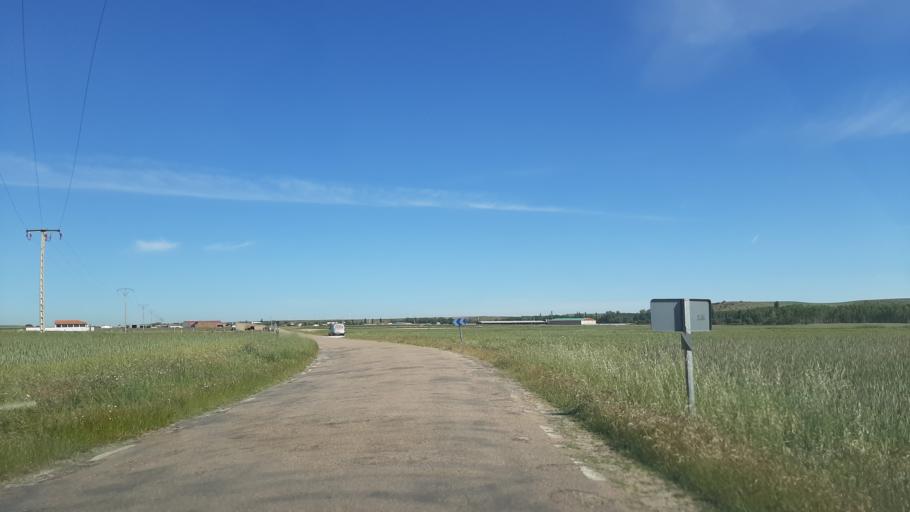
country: ES
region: Castille and Leon
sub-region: Provincia de Salamanca
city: Pedrosillo de Alba
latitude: 40.8118
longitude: -5.3849
